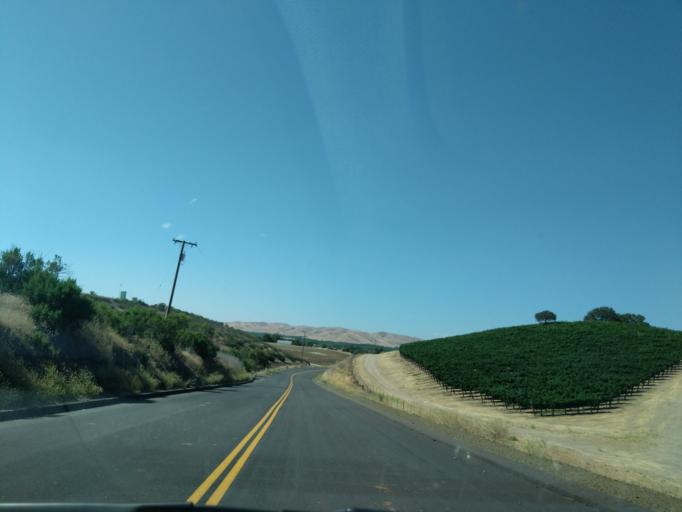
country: US
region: California
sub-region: San Luis Obispo County
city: San Miguel
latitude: 35.7049
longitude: -120.6402
